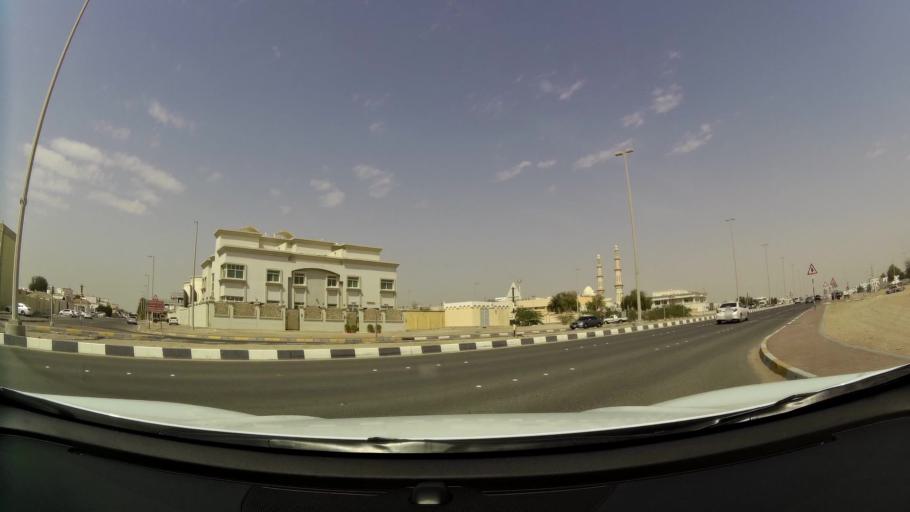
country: AE
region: Abu Dhabi
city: Abu Dhabi
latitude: 24.2977
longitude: 54.6463
